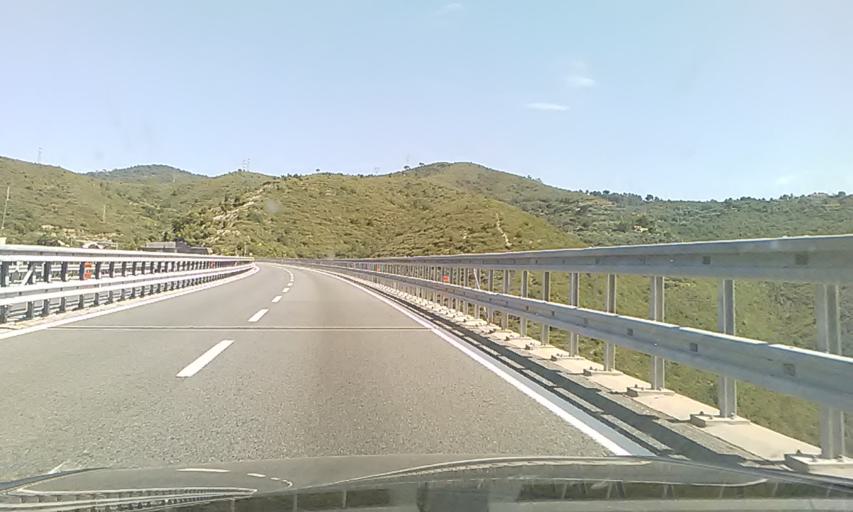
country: IT
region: Liguria
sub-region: Provincia di Savona
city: Laigueglia
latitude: 43.9922
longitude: 8.1371
